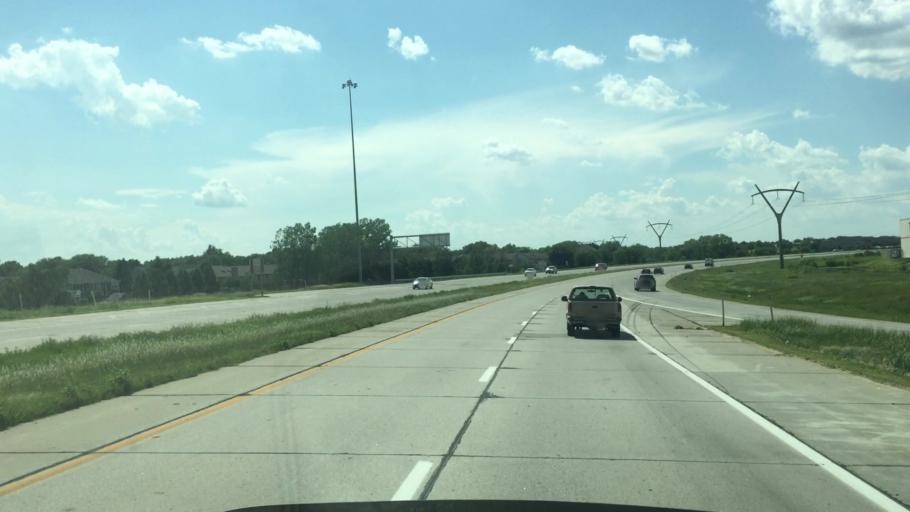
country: US
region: Kansas
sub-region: Sedgwick County
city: Bellaire
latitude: 37.7300
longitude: -97.2122
